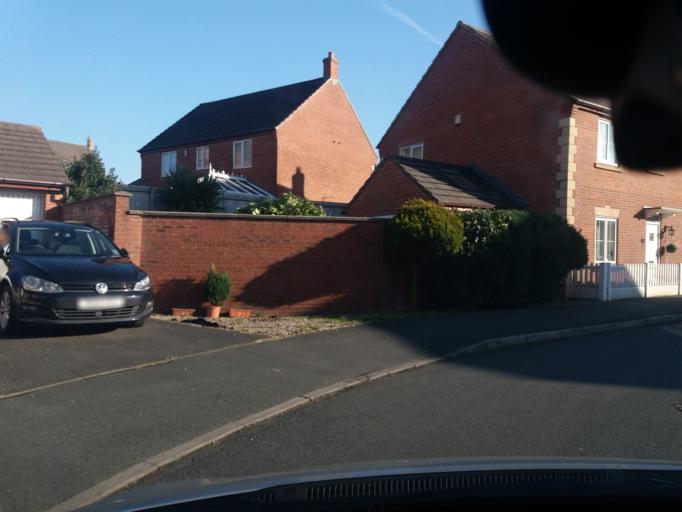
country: GB
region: England
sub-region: Lancashire
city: Adlington
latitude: 53.6201
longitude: -2.6081
